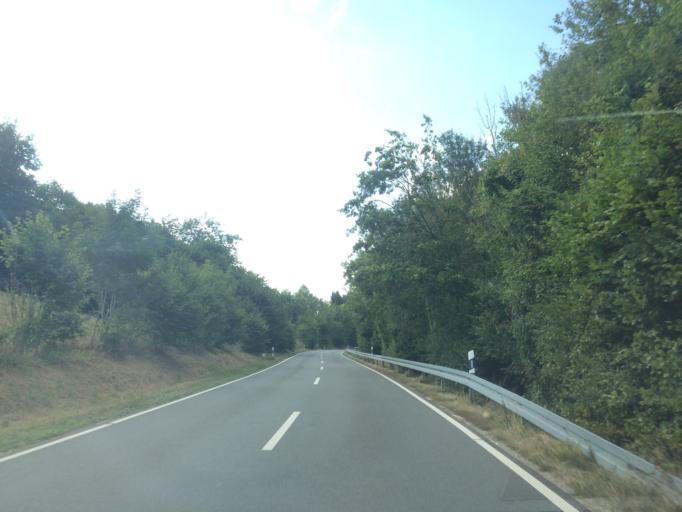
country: DE
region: Hesse
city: Trendelburg
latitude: 51.6089
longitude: 9.3746
